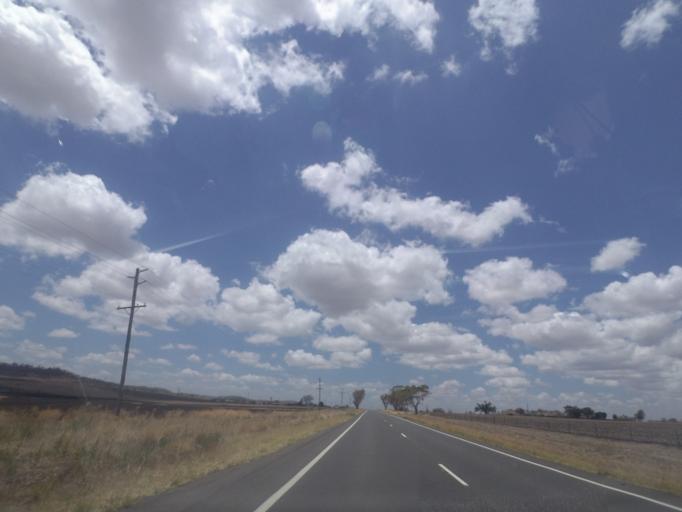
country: AU
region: Queensland
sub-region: Toowoomba
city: Top Camp
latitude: -27.7358
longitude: 151.9159
